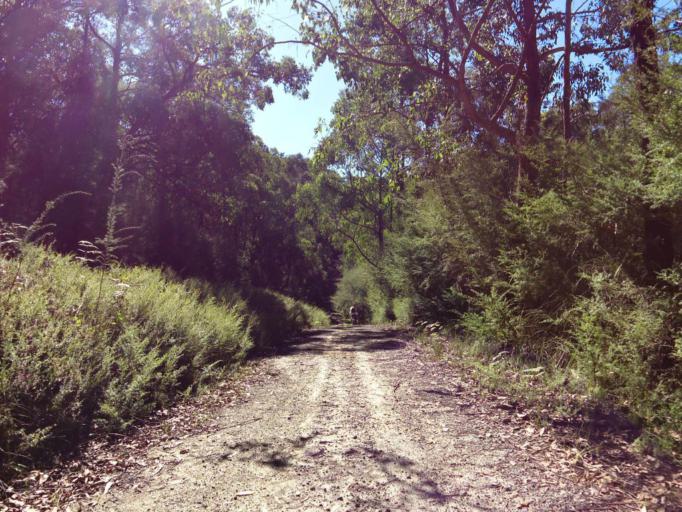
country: AU
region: Victoria
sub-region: Yarra Ranges
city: Launching Place
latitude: -37.7441
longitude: 145.5554
